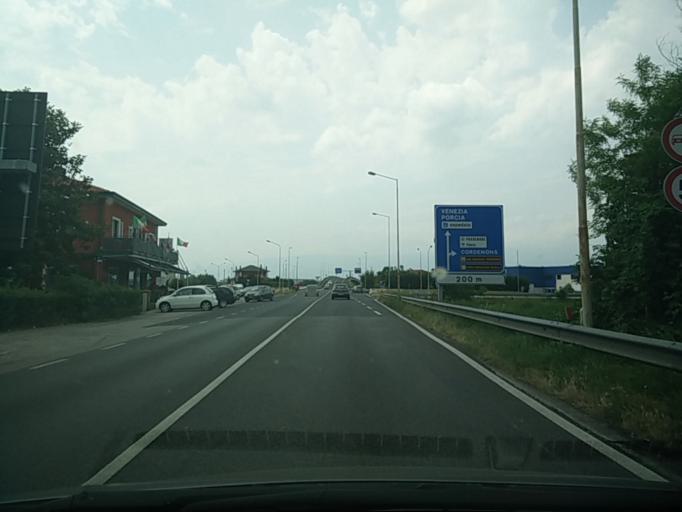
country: IT
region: Friuli Venezia Giulia
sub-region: Provincia di Pordenone
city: Cordenons
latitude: 45.9460
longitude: 12.6990
